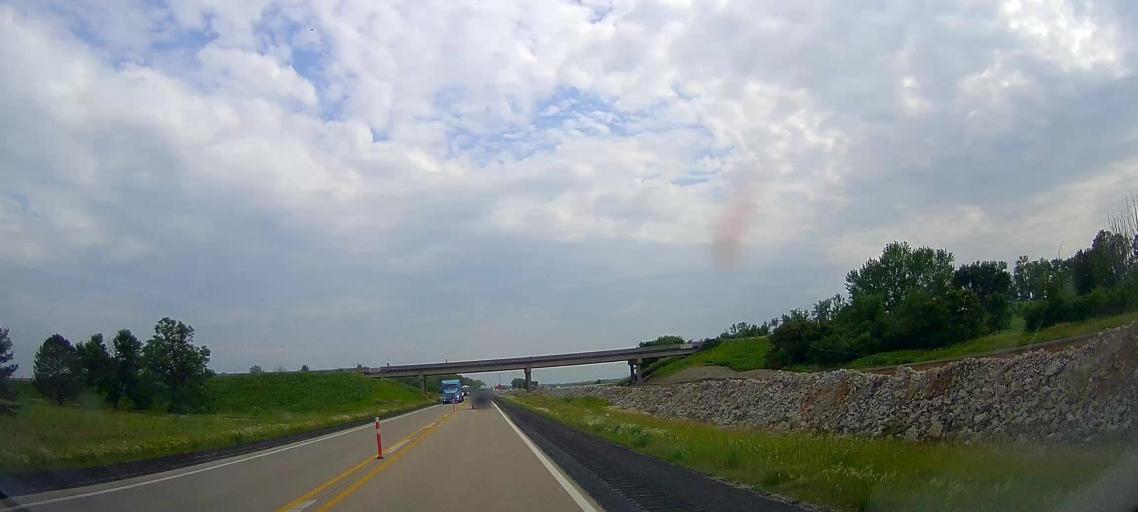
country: US
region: Nebraska
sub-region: Washington County
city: Blair
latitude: 41.7122
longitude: -96.0446
